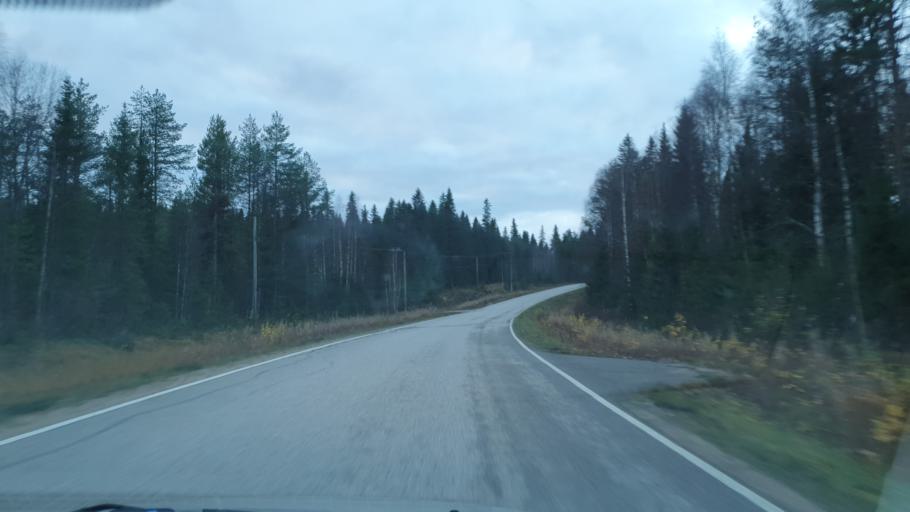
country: FI
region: Kainuu
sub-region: Kajaani
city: Ristijaervi
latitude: 64.4279
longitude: 28.3807
